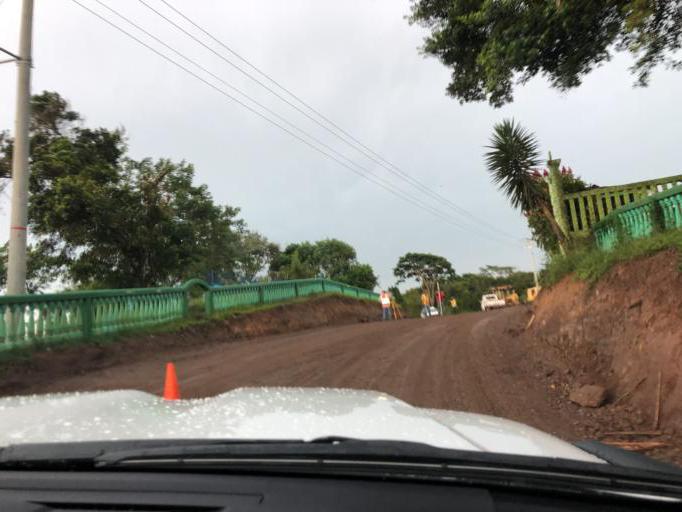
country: NI
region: Chontales
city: La Libertad
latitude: 12.2048
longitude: -85.1713
